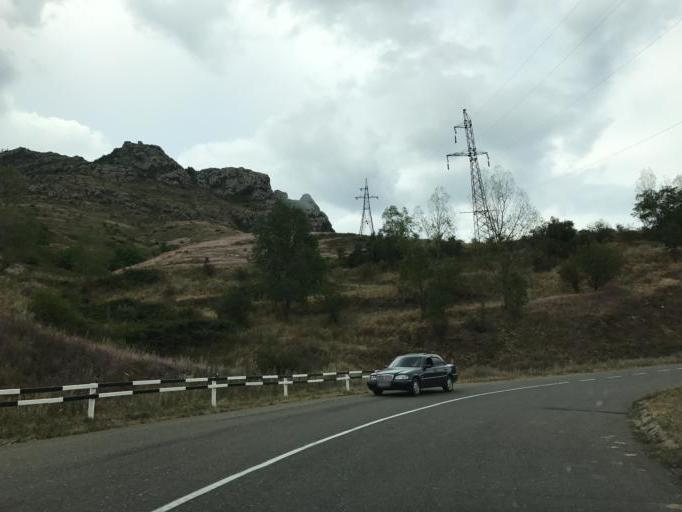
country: AZ
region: Susa
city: Shushi
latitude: 39.7185
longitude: 46.6773
